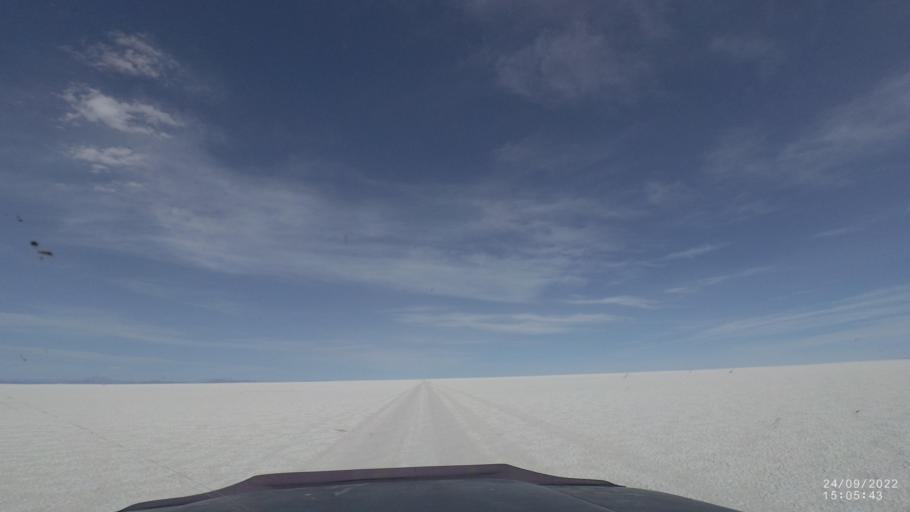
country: BO
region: Potosi
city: Colchani
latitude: -19.9083
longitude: -67.5152
